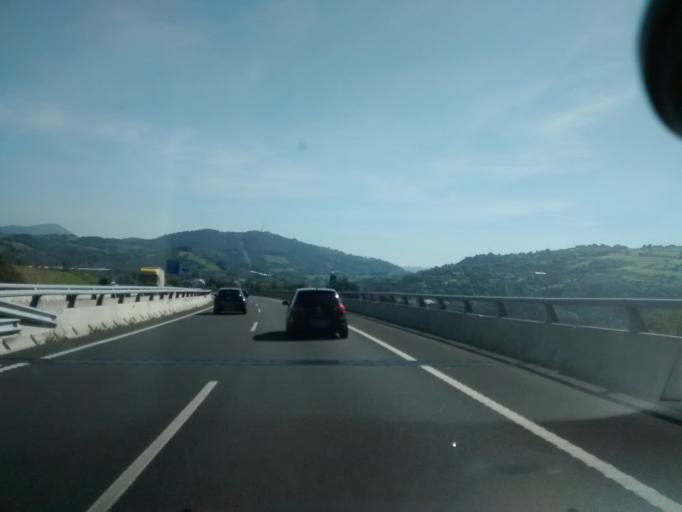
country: ES
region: Basque Country
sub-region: Provincia de Guipuzcoa
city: Hernani
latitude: 43.2771
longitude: -1.9660
